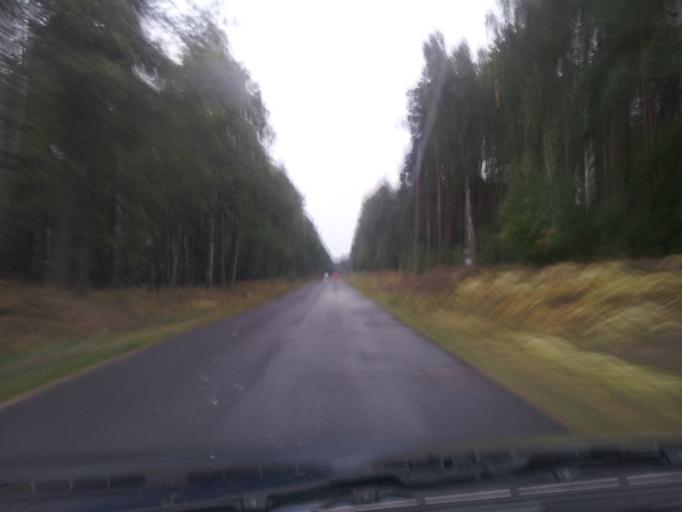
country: PL
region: Pomeranian Voivodeship
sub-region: Powiat bytowski
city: Czarna Dabrowka
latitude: 54.2837
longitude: 17.5971
